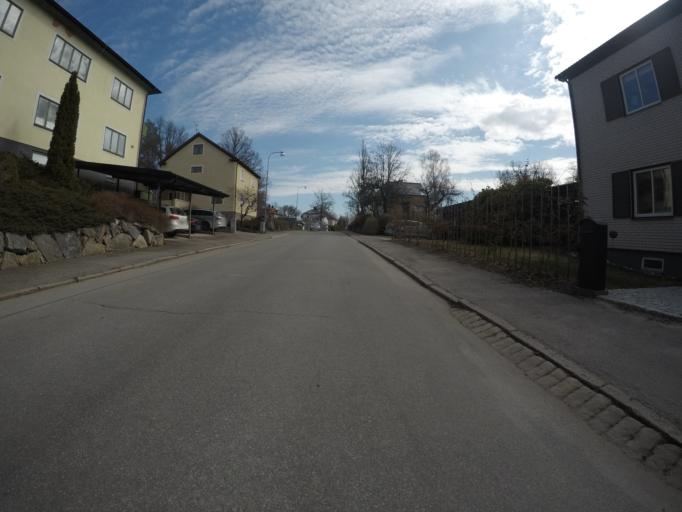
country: SE
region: Vaestmanland
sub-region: Vasteras
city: Vasteras
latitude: 59.6212
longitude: 16.5309
